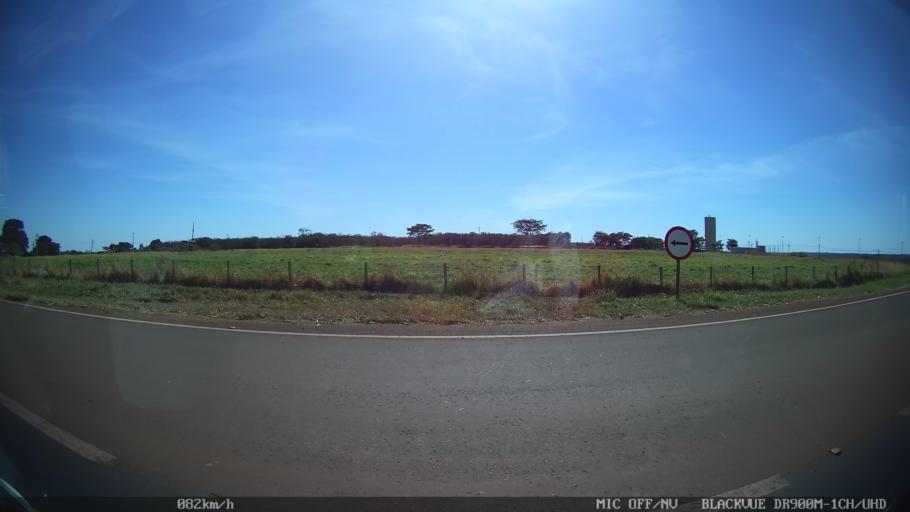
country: BR
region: Sao Paulo
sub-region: Barretos
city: Barretos
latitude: -20.5280
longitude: -48.5918
